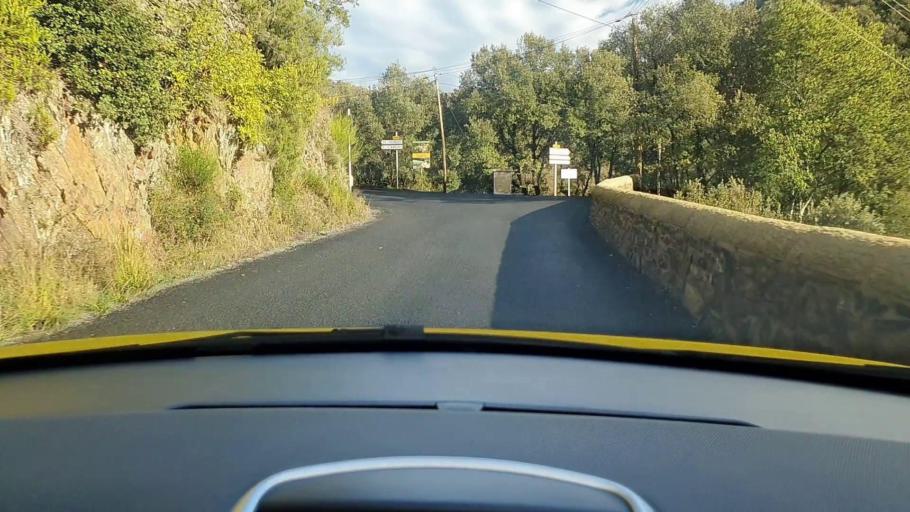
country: FR
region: Languedoc-Roussillon
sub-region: Departement du Gard
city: Sumene
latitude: 44.0201
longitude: 3.7306
